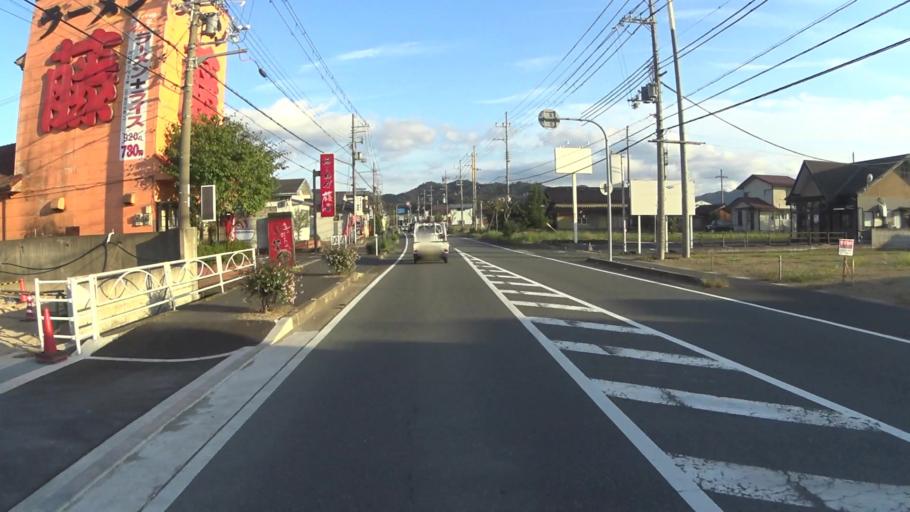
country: JP
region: Kyoto
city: Miyazu
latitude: 35.5869
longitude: 135.0969
